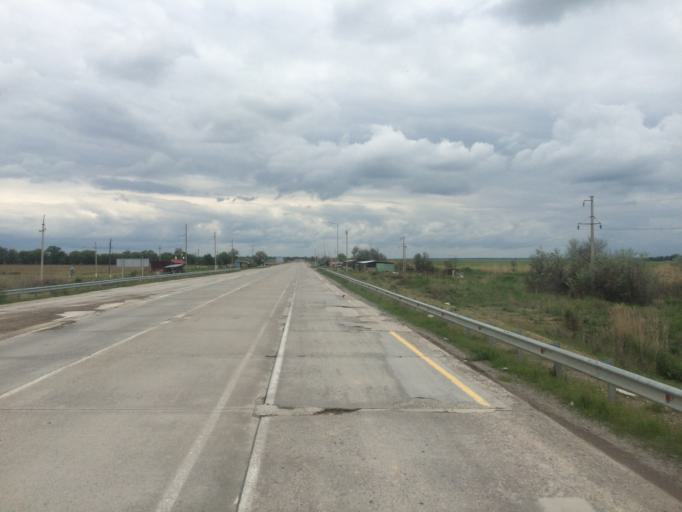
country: KG
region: Chuy
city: Sokuluk
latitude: 43.2724
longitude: 74.2372
